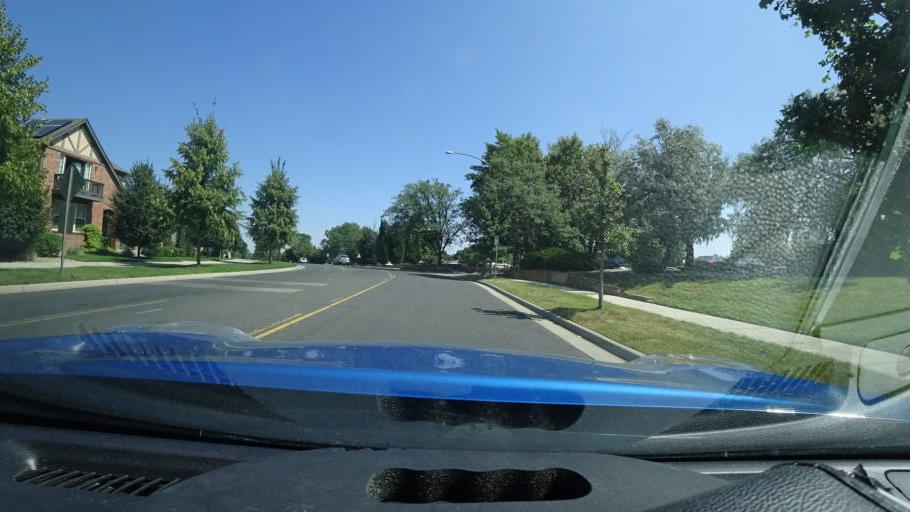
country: US
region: Colorado
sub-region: Adams County
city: Aurora
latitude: 39.7192
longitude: -104.8755
